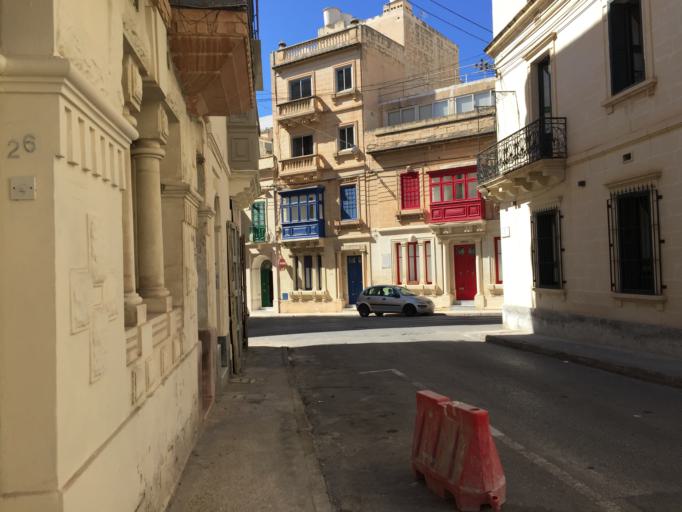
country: MT
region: Tas-Sliema
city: Sliema
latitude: 35.9146
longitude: 14.4996
